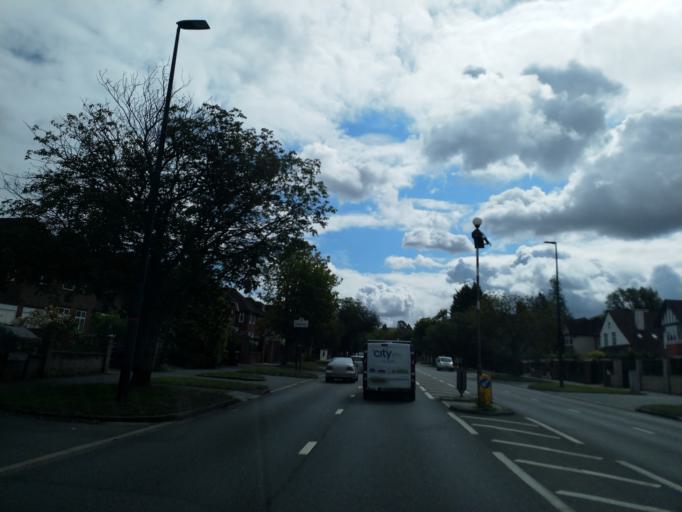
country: GB
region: England
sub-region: Greater London
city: Belsize Park
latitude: 51.5832
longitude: -0.1658
